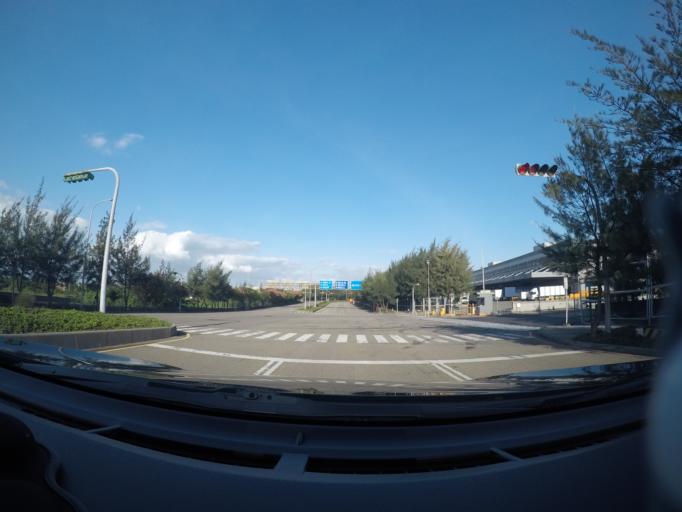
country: TW
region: Taiwan
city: Taoyuan City
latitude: 25.0996
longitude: 121.2522
